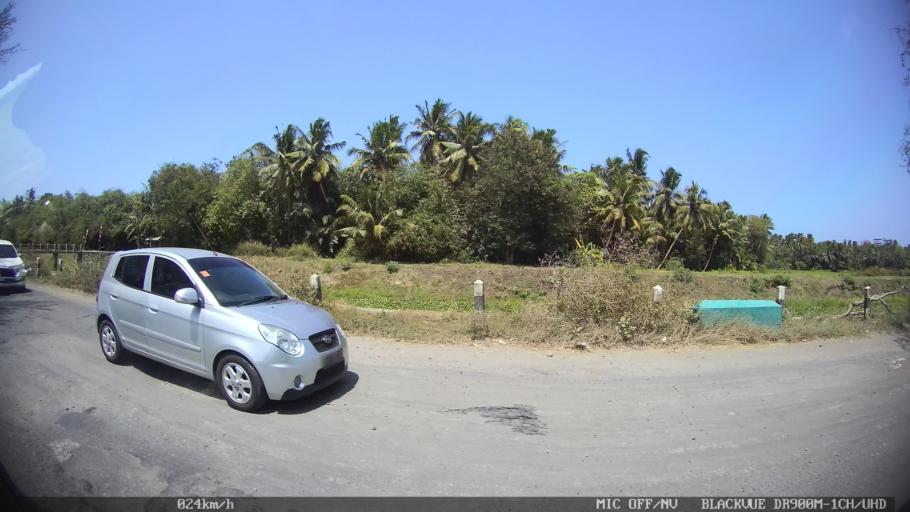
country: ID
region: Daerah Istimewa Yogyakarta
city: Srandakan
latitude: -7.9478
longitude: 110.1808
